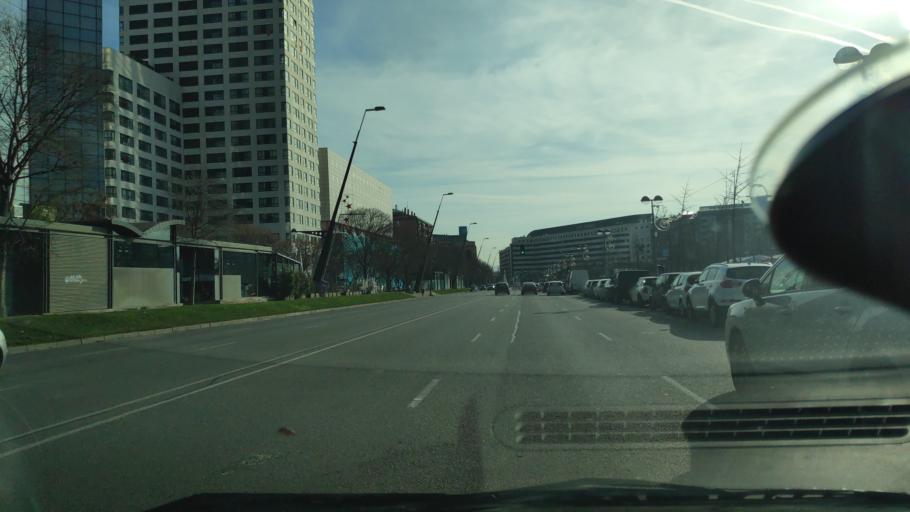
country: ES
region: Catalonia
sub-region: Provincia de Barcelona
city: Sabadell
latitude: 41.5532
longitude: 2.0977
